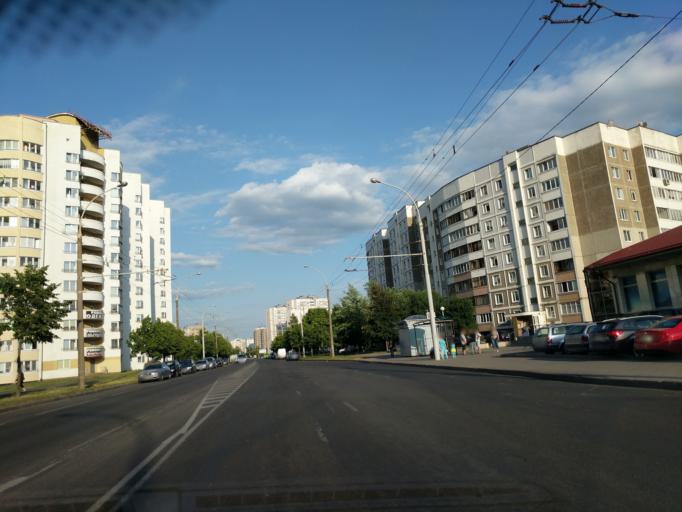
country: BY
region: Minsk
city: Malinovka
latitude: 53.8516
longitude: 27.4520
